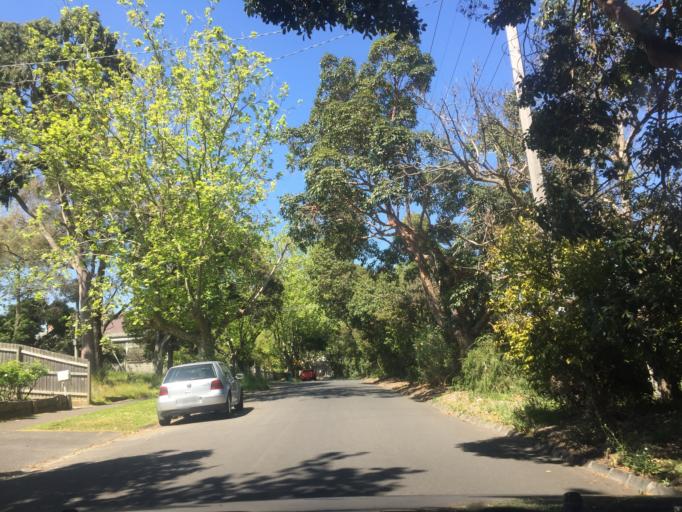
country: AU
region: Victoria
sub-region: Boroondara
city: Canterbury
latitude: -37.8255
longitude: 145.0736
